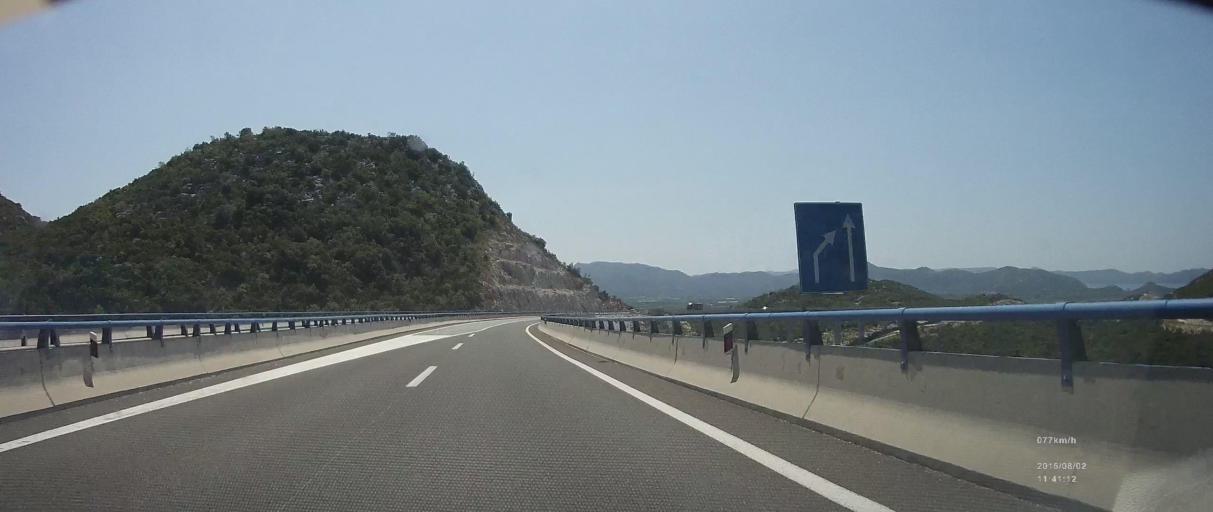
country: HR
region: Dubrovacko-Neretvanska
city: Komin
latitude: 43.0661
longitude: 17.4946
